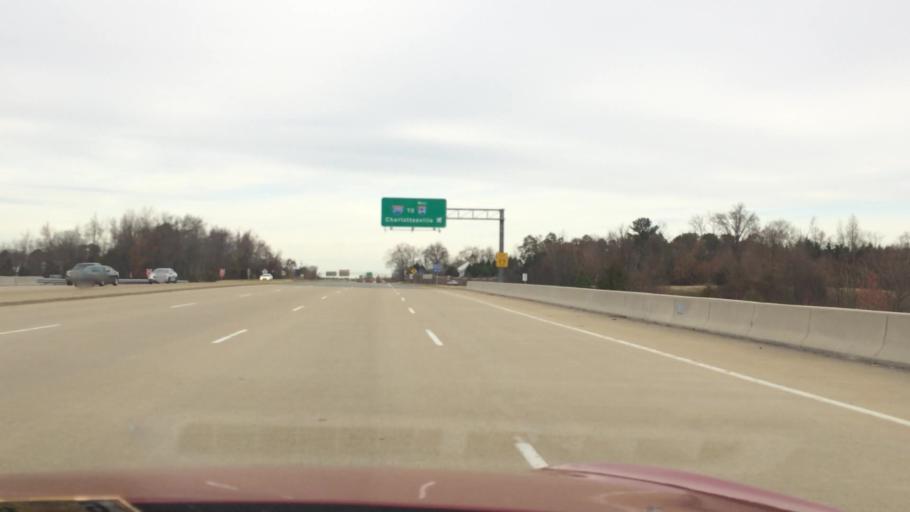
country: US
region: Virginia
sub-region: Henrico County
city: Chamberlayne
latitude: 37.6589
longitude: -77.4599
